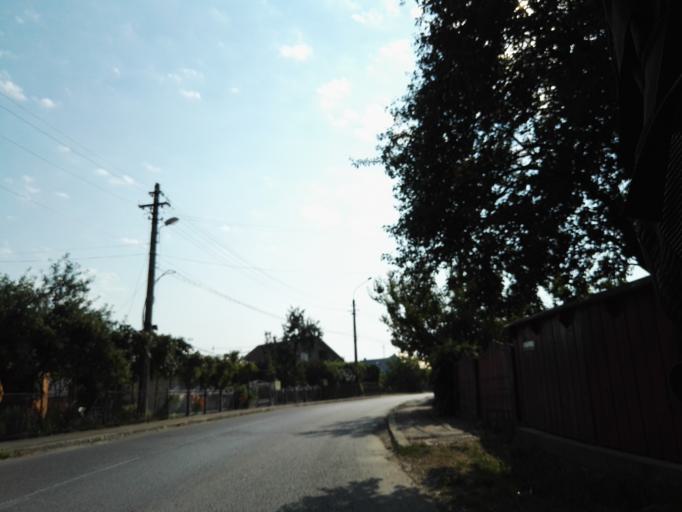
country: RO
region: Suceava
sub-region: Comuna Radaseni
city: Radaseni
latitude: 47.4686
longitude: 26.2738
